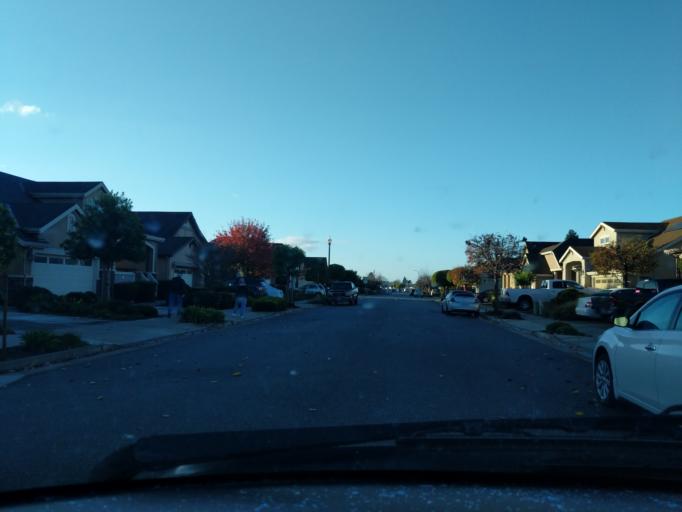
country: US
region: California
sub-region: Monterey County
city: Pajaro
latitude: 36.9228
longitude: -121.7364
